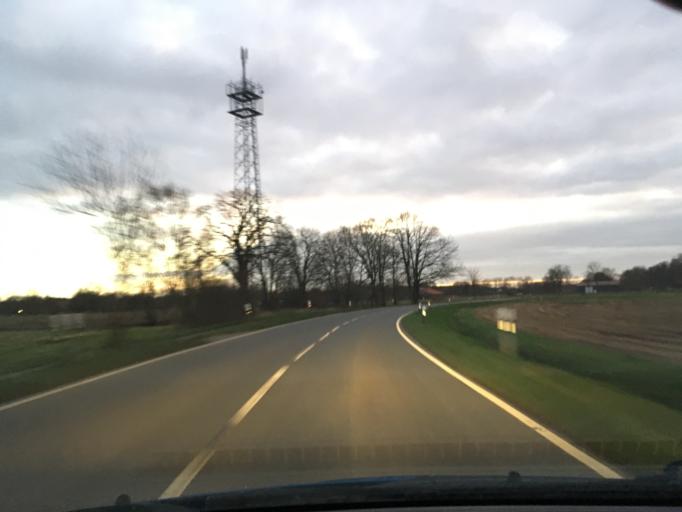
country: DE
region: Lower Saxony
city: Barum
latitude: 53.3582
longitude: 10.4103
